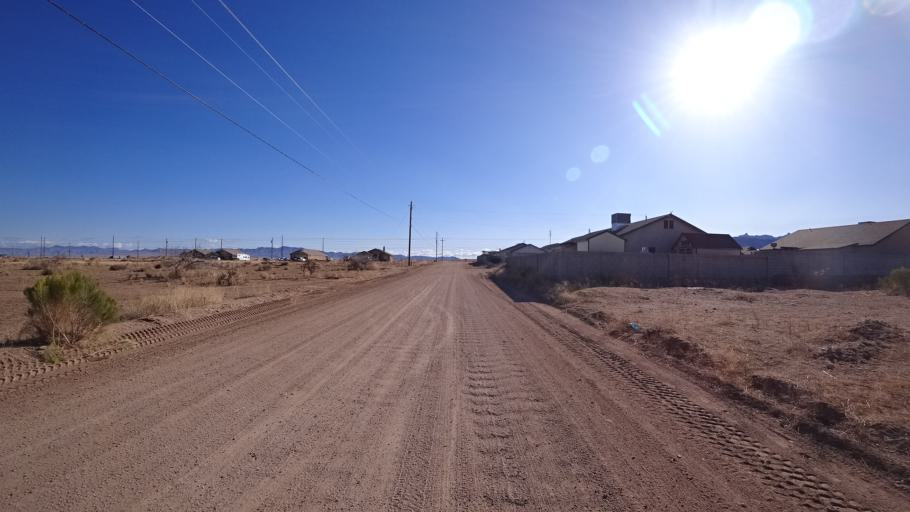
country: US
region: Arizona
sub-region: Mohave County
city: Kingman
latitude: 35.2121
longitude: -113.9957
